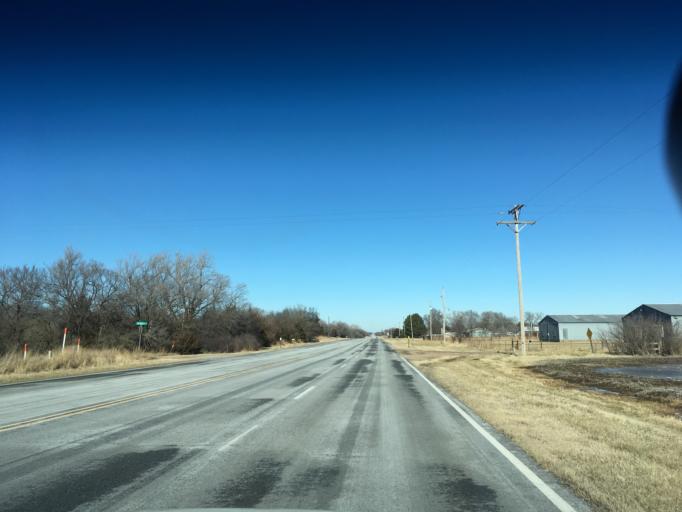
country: US
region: Kansas
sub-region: Harvey County
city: Sedgwick
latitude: 37.9260
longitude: -97.3363
